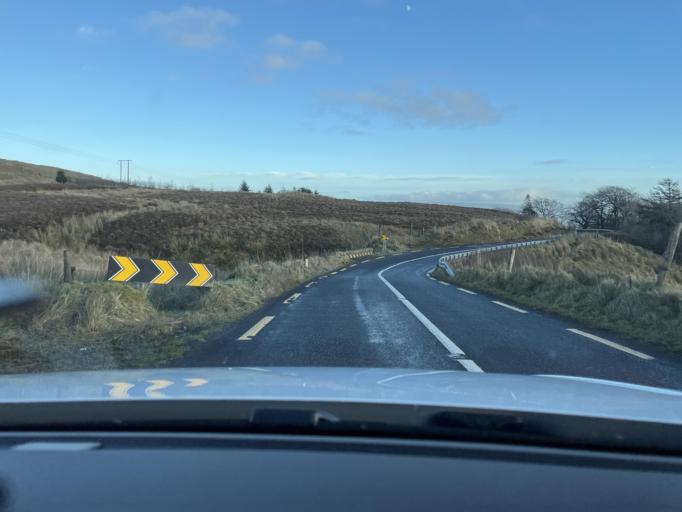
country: IE
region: Ulster
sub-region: An Cabhan
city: Ballyconnell
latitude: 54.1669
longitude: -7.8079
